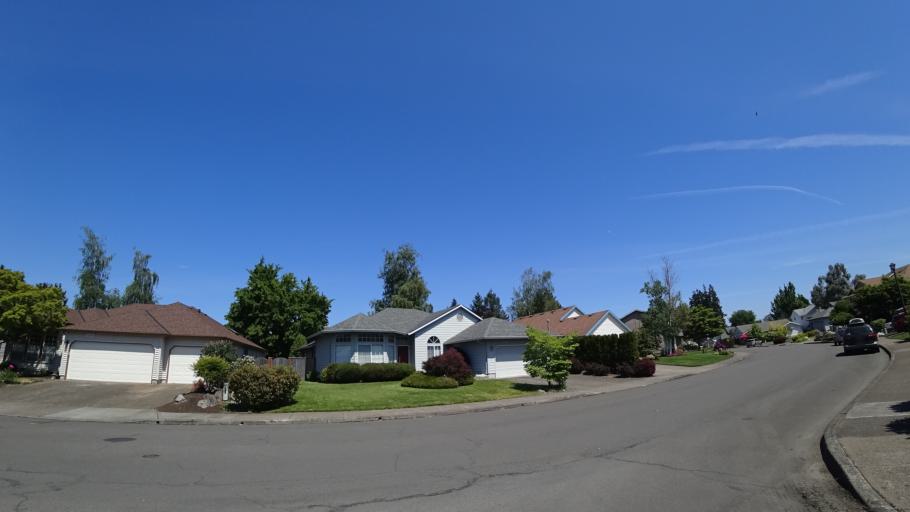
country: US
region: Oregon
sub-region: Washington County
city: King City
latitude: 45.4356
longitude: -122.8073
